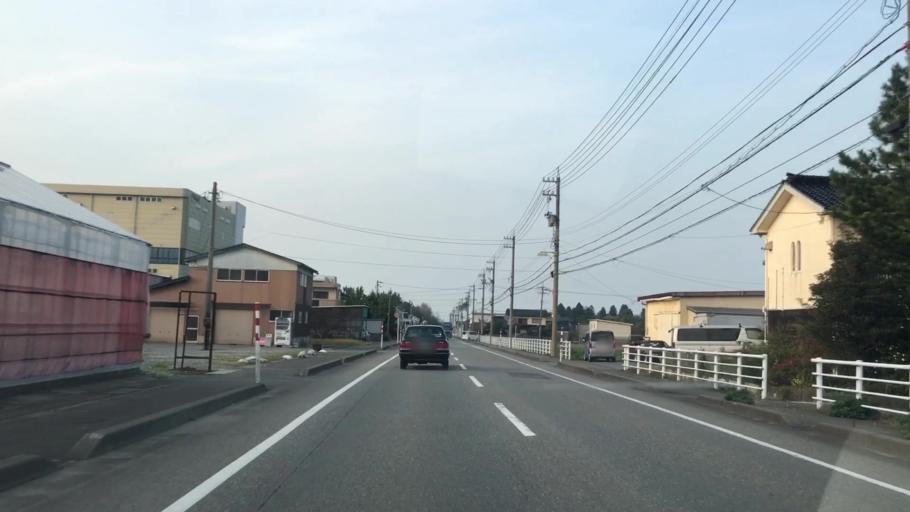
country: JP
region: Toyama
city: Yatsuomachi-higashikumisaka
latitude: 36.5858
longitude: 137.1914
